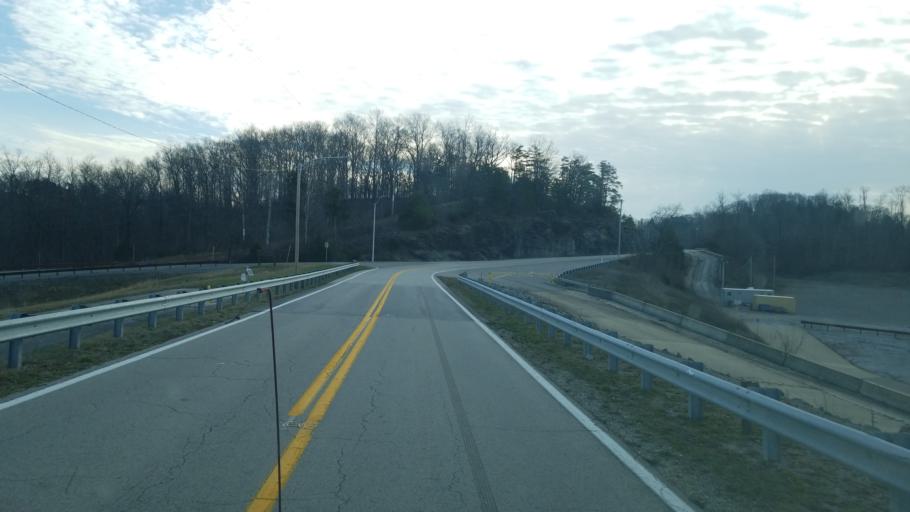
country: US
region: Kentucky
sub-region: Russell County
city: Jamestown
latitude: 36.8722
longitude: -85.1325
